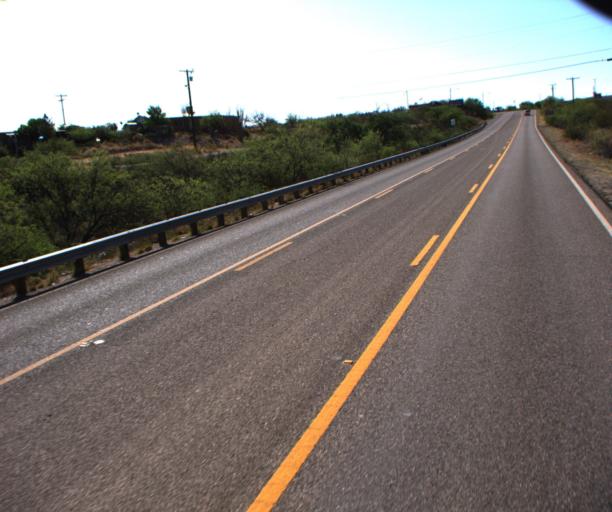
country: US
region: Arizona
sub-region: Cochise County
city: Tombstone
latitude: 31.7215
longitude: -110.0723
